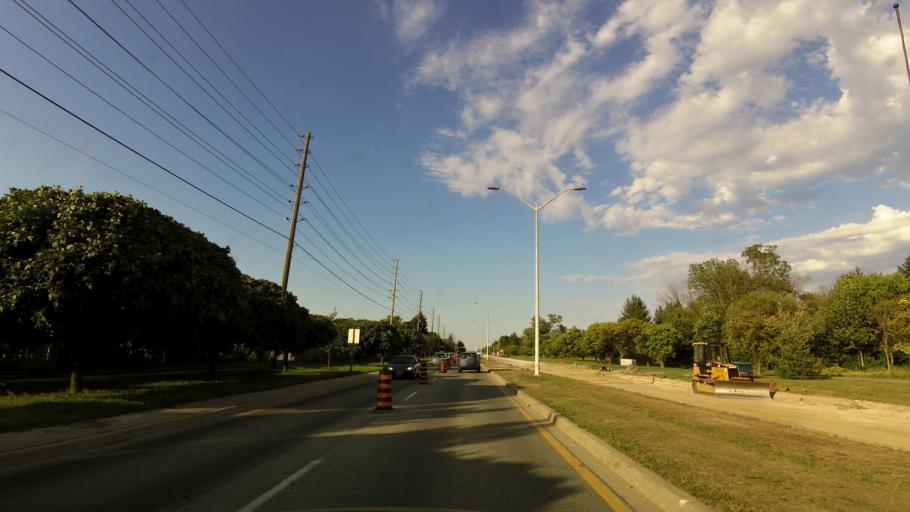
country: CA
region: Ontario
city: Mississauga
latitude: 43.5625
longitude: -79.6207
